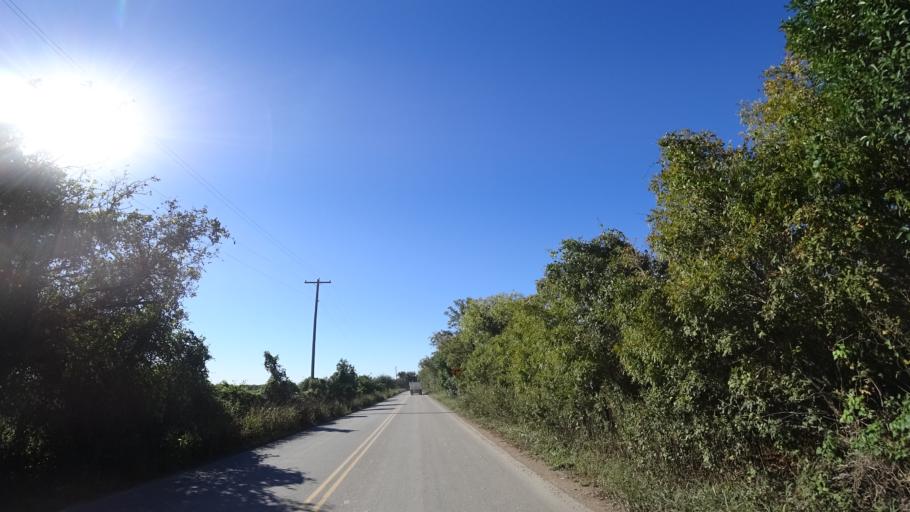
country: US
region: Texas
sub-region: Travis County
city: Austin
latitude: 30.2437
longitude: -97.6802
